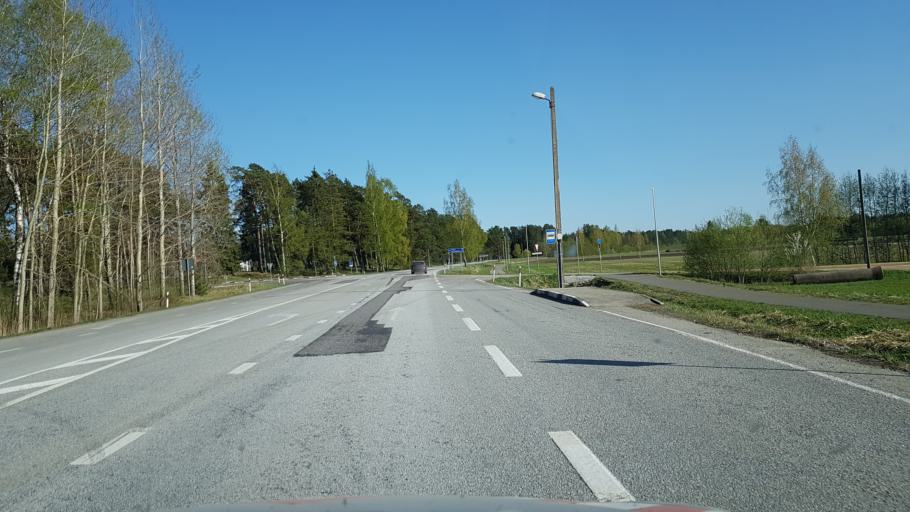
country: EE
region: Paernumaa
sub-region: Paikuse vald
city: Paikuse
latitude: 58.3583
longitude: 24.6587
